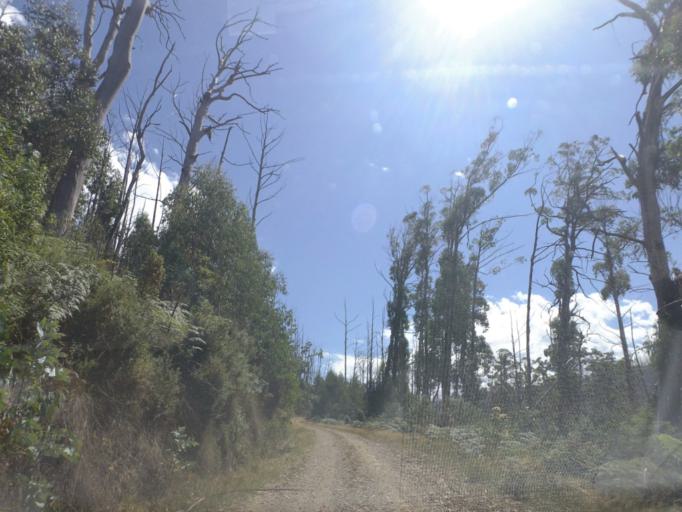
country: AU
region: Victoria
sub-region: Murrindindi
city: Alexandra
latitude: -37.4784
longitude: 145.8402
